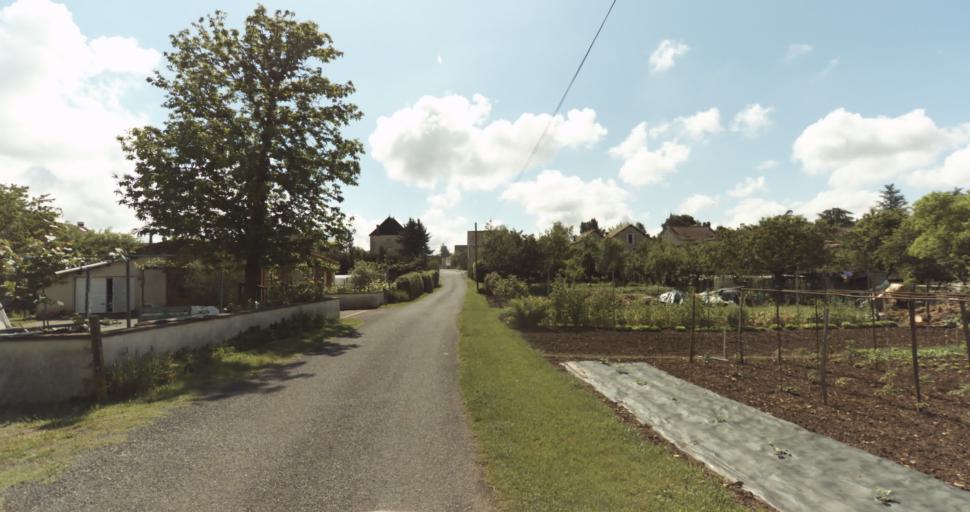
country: FR
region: Aquitaine
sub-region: Departement de la Dordogne
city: Le Bugue
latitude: 44.8461
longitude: 0.9061
